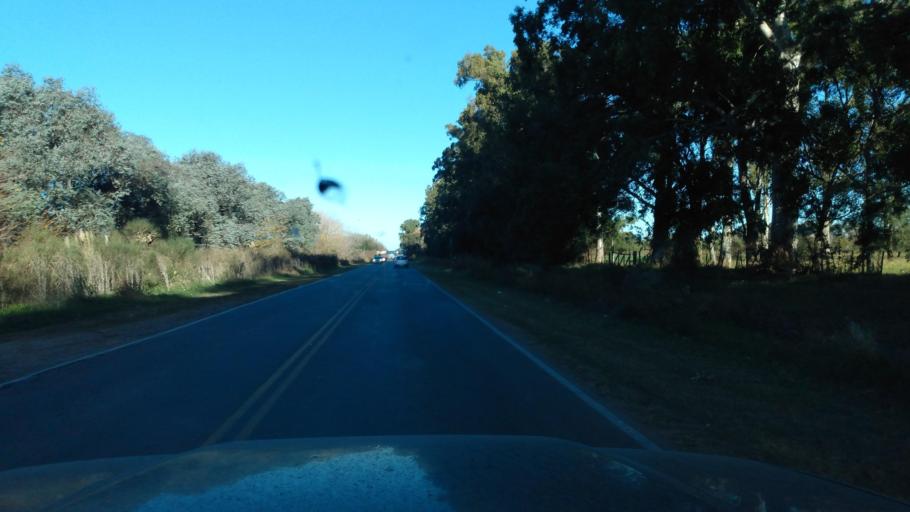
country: AR
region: Buenos Aires
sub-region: Partido de Lujan
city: Lujan
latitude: -34.5319
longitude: -59.1670
